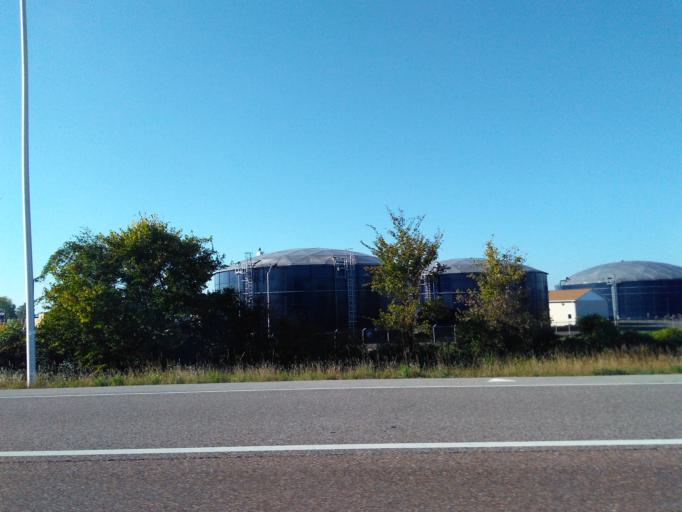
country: US
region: Illinois
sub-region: Saint Clair County
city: Caseyville
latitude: 38.6692
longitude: -90.0311
